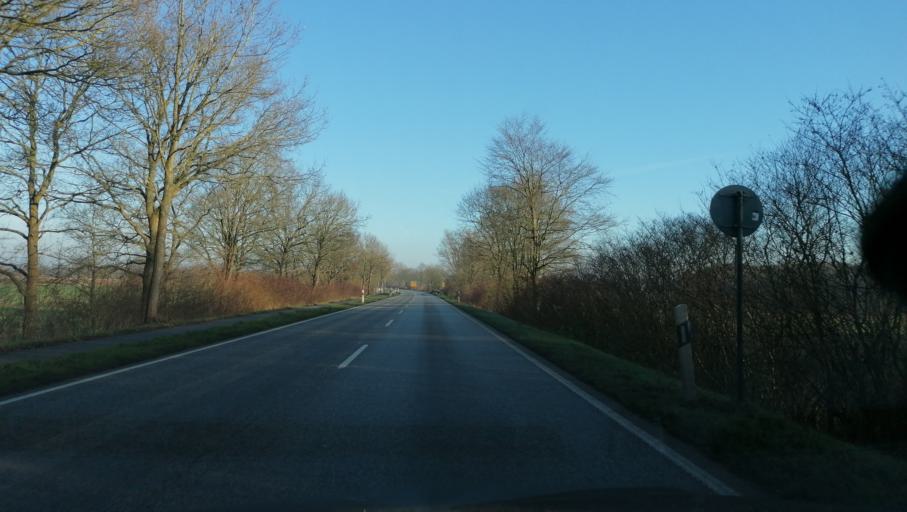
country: DE
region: Schleswig-Holstein
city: Sarzbuttel
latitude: 54.1026
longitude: 9.1892
